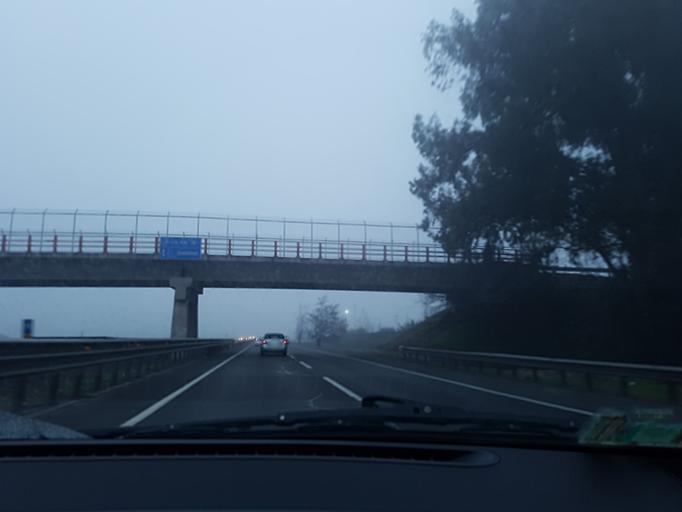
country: CL
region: Santiago Metropolitan
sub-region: Provincia de Talagante
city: Penaflor
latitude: -33.5384
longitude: -70.8025
